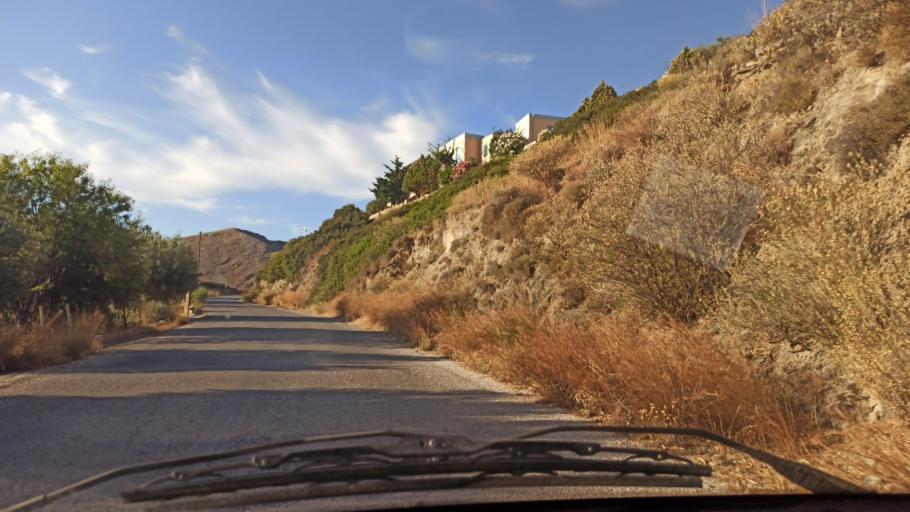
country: GR
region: South Aegean
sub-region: Nomos Kykladon
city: Ano Syros
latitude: 37.4427
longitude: 24.9124
